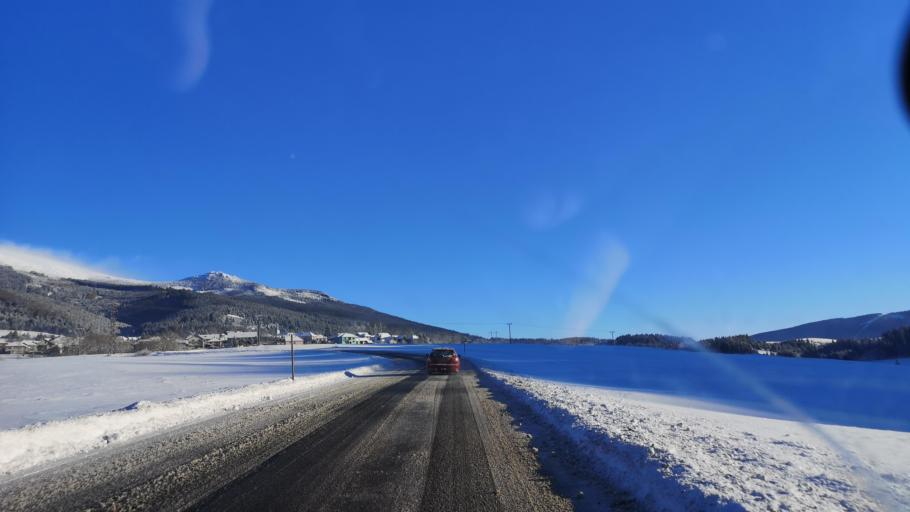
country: SK
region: Banskobystricky
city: Revuca
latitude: 48.8311
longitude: 20.1218
